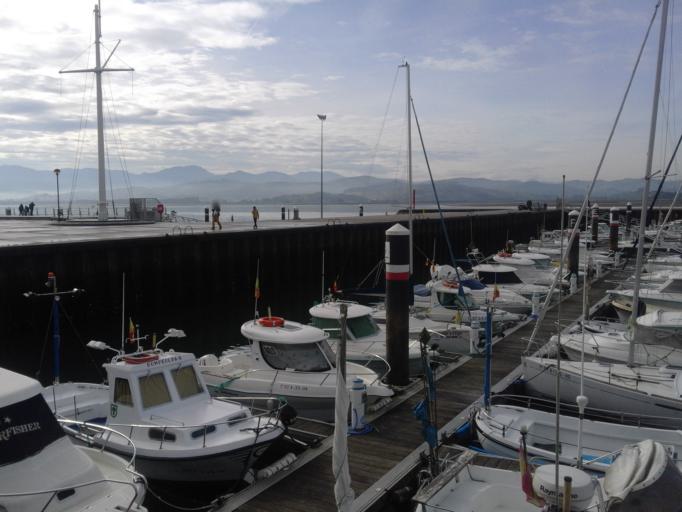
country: ES
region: Cantabria
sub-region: Provincia de Cantabria
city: Santona
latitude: 43.4403
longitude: -3.4609
